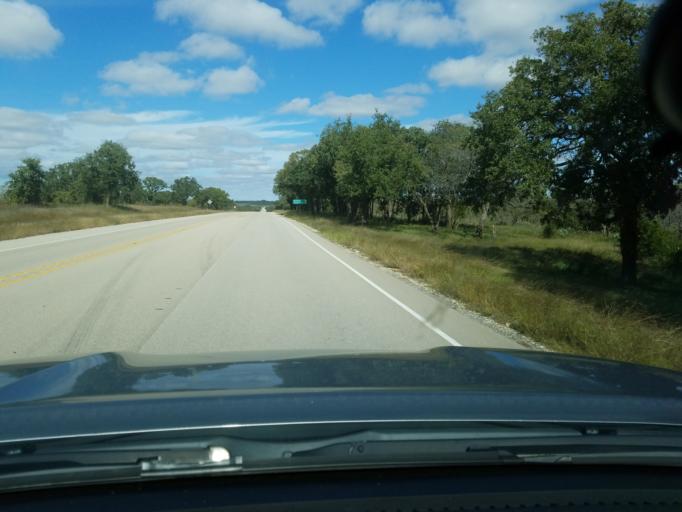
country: US
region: Texas
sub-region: Hamilton County
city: Hamilton
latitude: 31.5955
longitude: -98.1572
